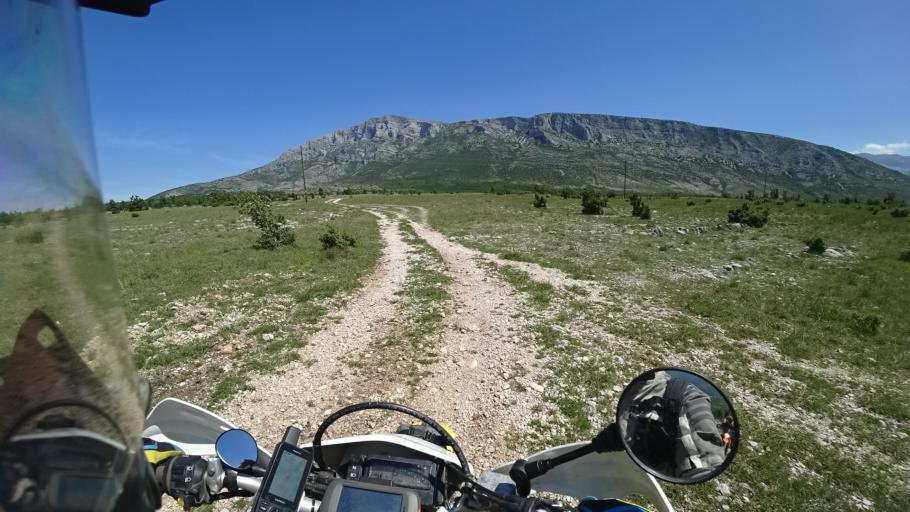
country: BA
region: Federation of Bosnia and Herzegovina
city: Bosansko Grahovo
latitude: 44.0060
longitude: 16.3762
